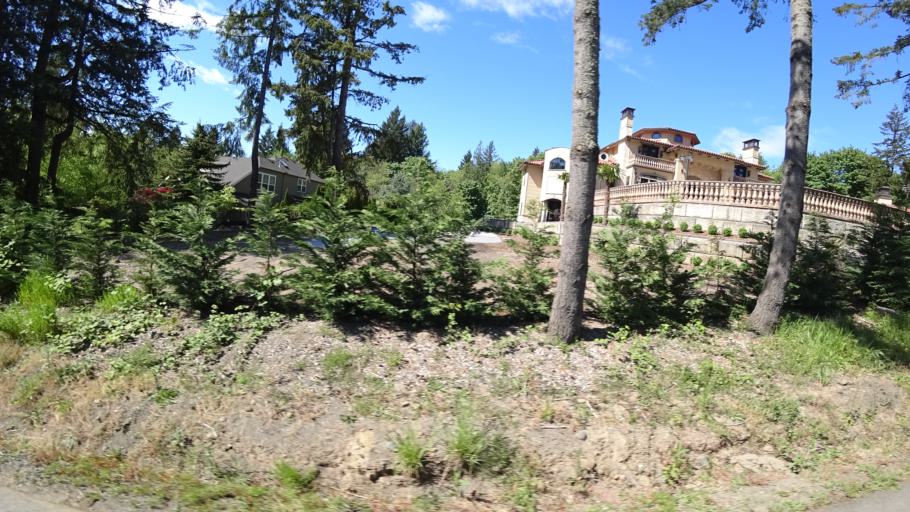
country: US
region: Oregon
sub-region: Washington County
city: Cedar Mill
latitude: 45.5500
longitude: -122.7915
